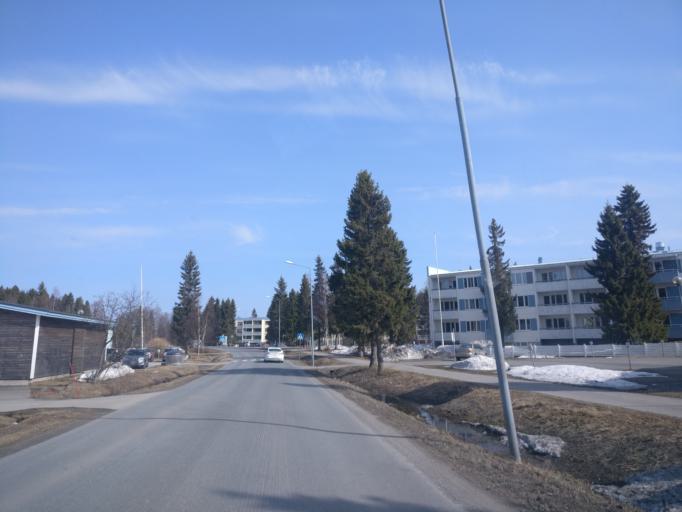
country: FI
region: Lapland
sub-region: Kemi-Tornio
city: Kemi
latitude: 65.7276
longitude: 24.6245
